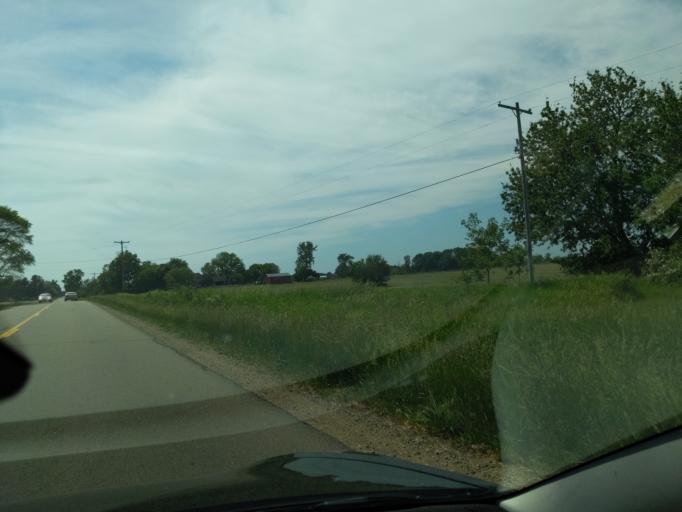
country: US
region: Michigan
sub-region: Eaton County
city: Grand Ledge
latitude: 42.7119
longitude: -84.7688
